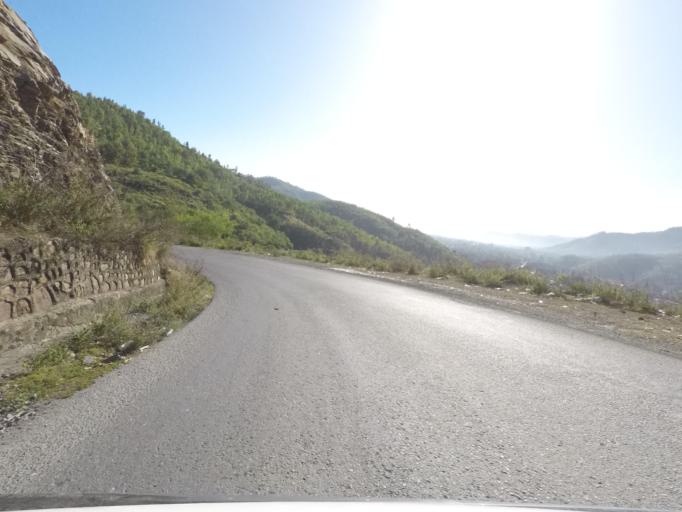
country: TL
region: Dili
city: Dili
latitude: -8.5597
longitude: 125.6409
